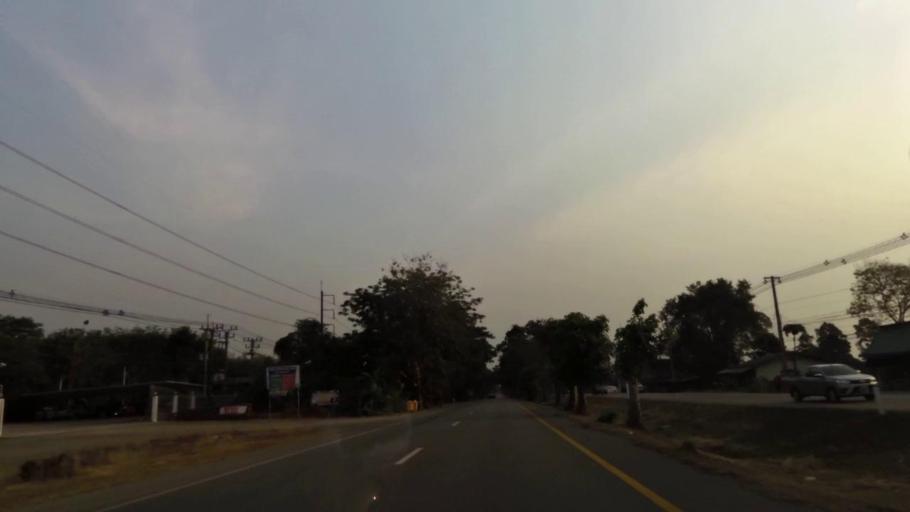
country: TH
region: Chanthaburi
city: Khlung
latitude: 12.4958
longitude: 102.1725
